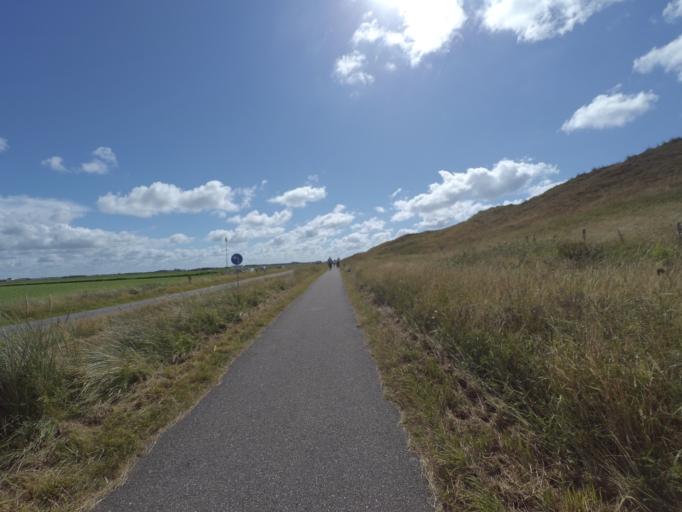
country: NL
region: North Holland
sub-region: Gemeente Texel
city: Den Burg
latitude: 53.1206
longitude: 4.8047
